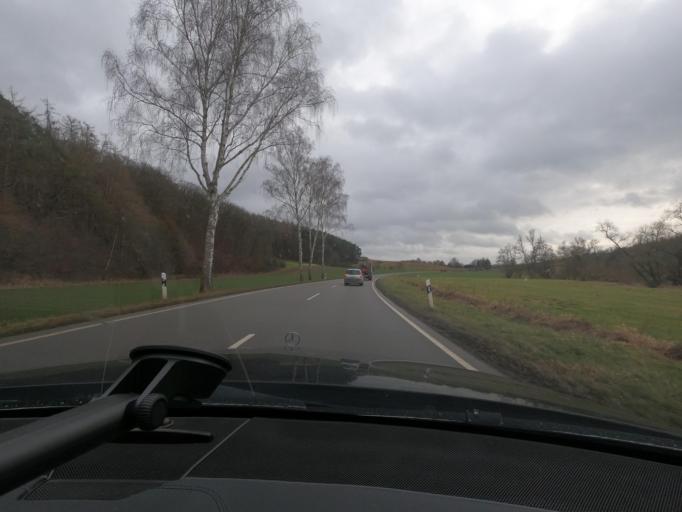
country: DE
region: Hesse
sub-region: Regierungsbezirk Kassel
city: Volkmarsen
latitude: 51.3992
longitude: 9.1409
